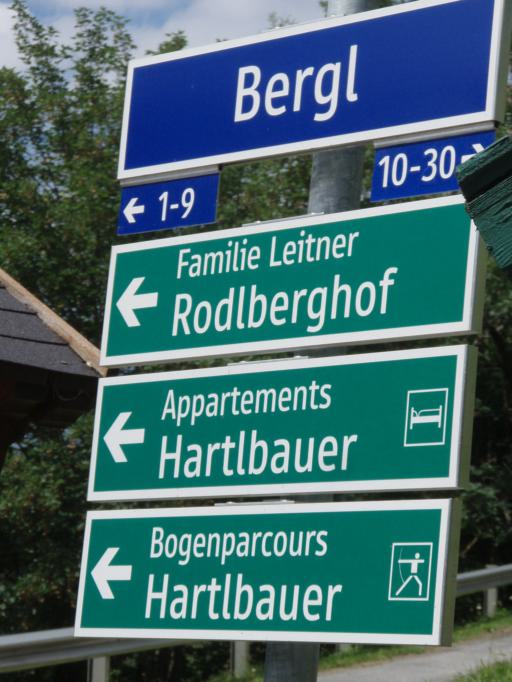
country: AT
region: Salzburg
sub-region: Politischer Bezirk Sankt Johann im Pongau
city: Dorfgastein
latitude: 47.2494
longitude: 13.1107
